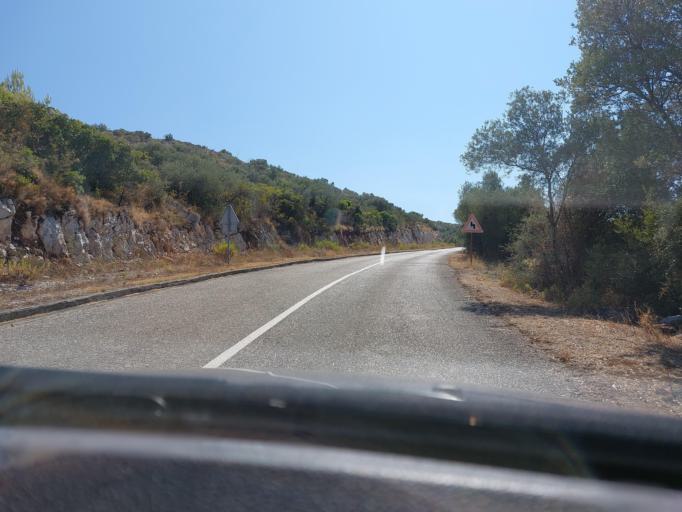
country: HR
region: Dubrovacko-Neretvanska
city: Smokvica
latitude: 42.7463
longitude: 16.8753
